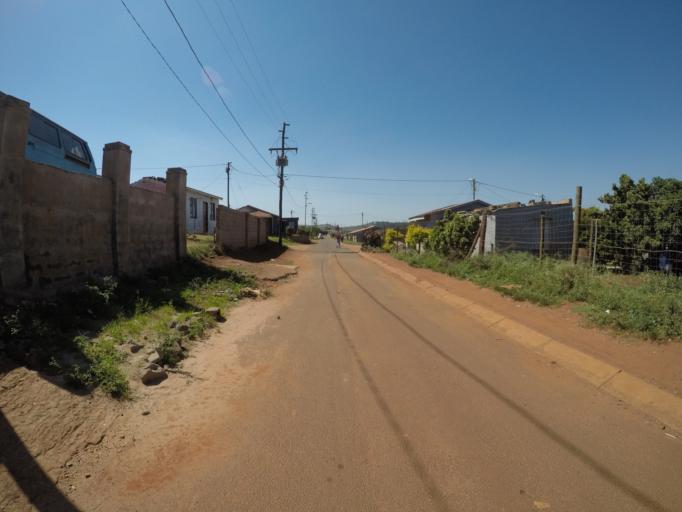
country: ZA
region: KwaZulu-Natal
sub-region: uThungulu District Municipality
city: Empangeni
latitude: -28.7710
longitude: 31.8781
